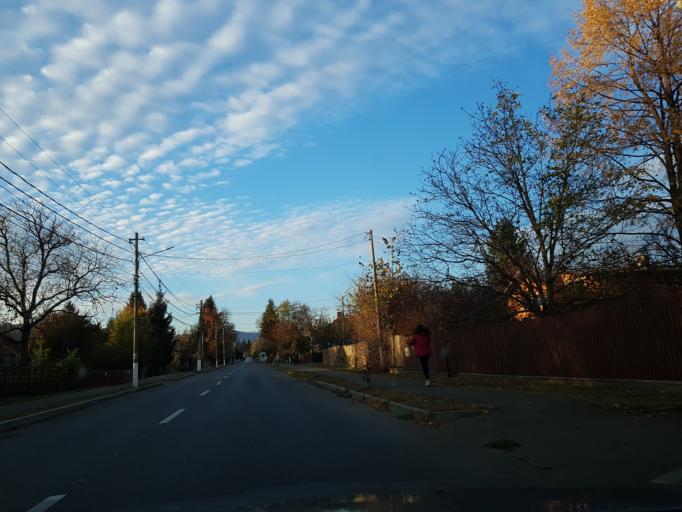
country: RO
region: Prahova
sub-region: Oras Breaza
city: Breaza de Sus
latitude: 45.1907
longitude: 25.6593
